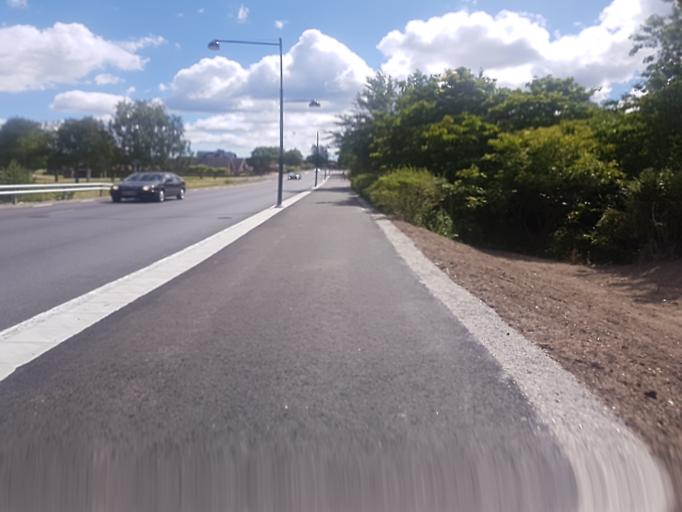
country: SE
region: Soedermanland
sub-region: Gnesta Kommun
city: Gnesta
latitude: 59.0468
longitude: 17.3203
